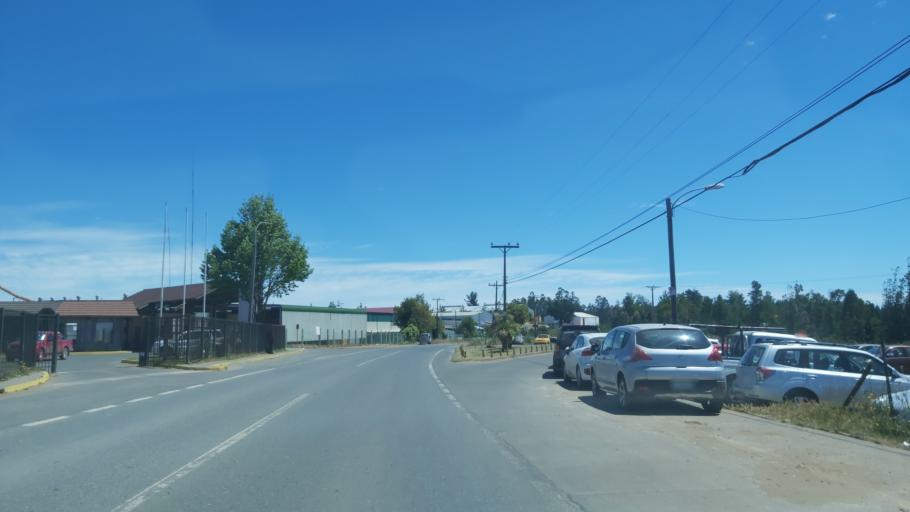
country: CL
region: Maule
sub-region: Provincia de Talca
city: Constitucion
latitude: -35.3735
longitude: -72.4150
